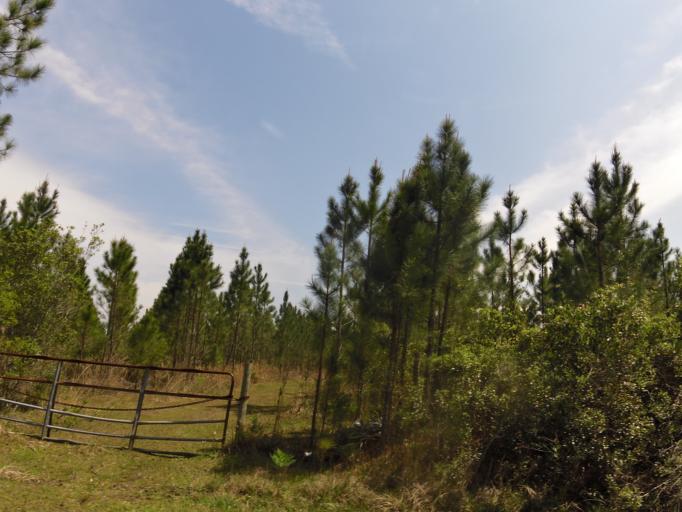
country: US
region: Florida
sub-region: Nassau County
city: Yulee
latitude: 30.5028
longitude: -81.6631
